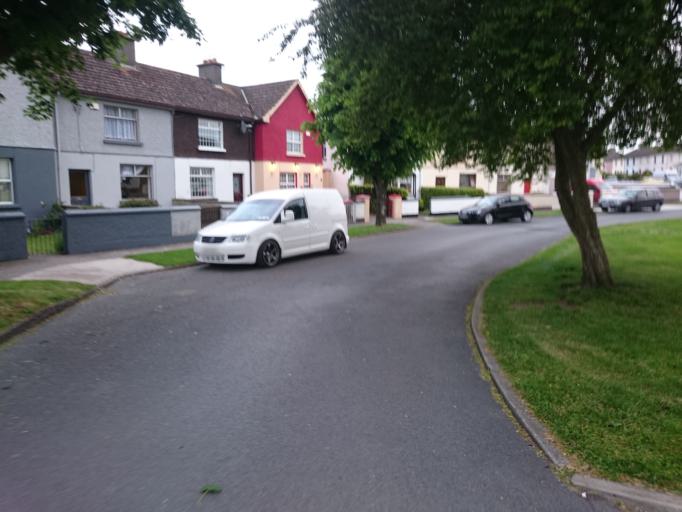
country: IE
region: Leinster
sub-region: Kilkenny
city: Kilkenny
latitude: 52.6518
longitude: -7.2642
